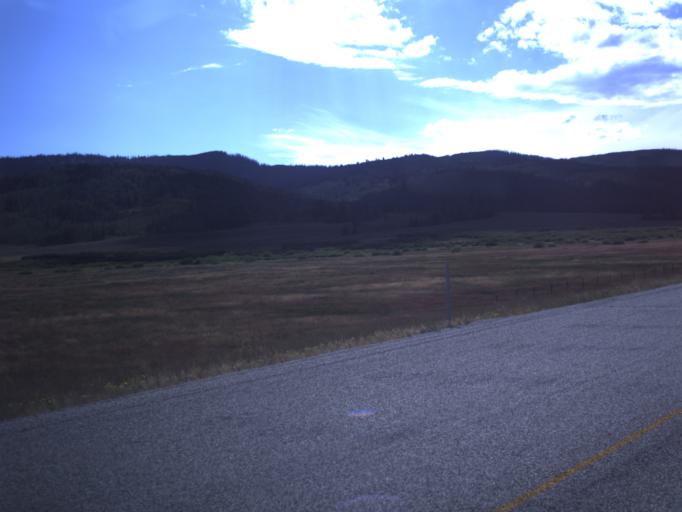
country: US
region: Utah
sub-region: Wasatch County
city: Heber
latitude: 40.2795
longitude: -111.2213
